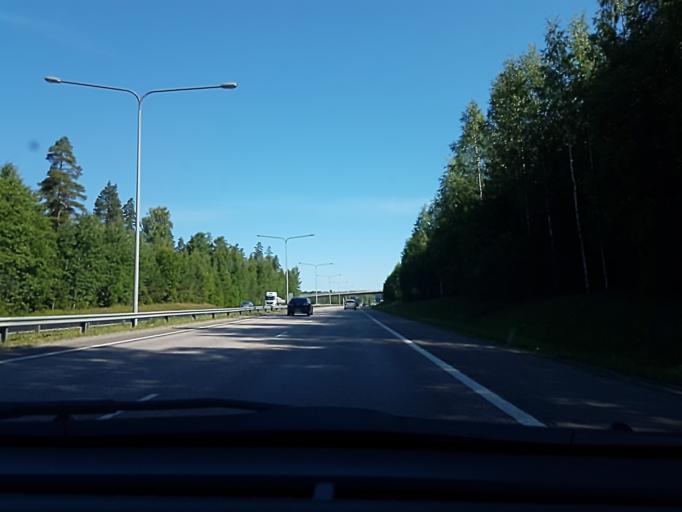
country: FI
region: Uusimaa
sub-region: Helsinki
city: Vantaa
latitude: 60.3305
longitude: 24.9990
